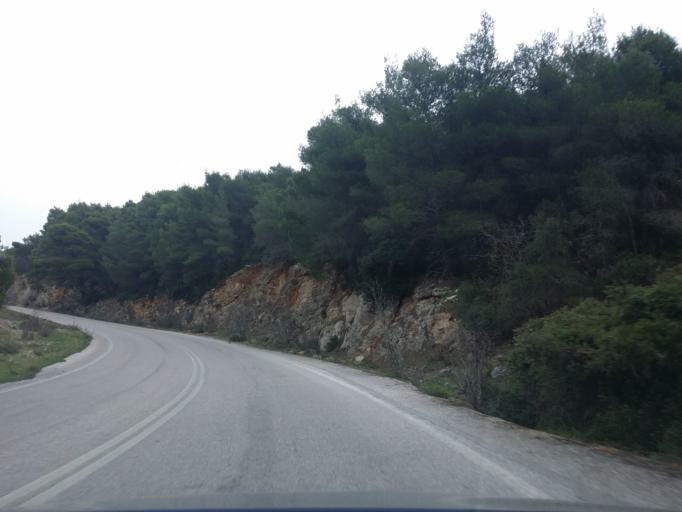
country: GR
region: Attica
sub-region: Nomarchia Dytikis Attikis
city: Vilia
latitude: 38.1417
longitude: 23.2629
